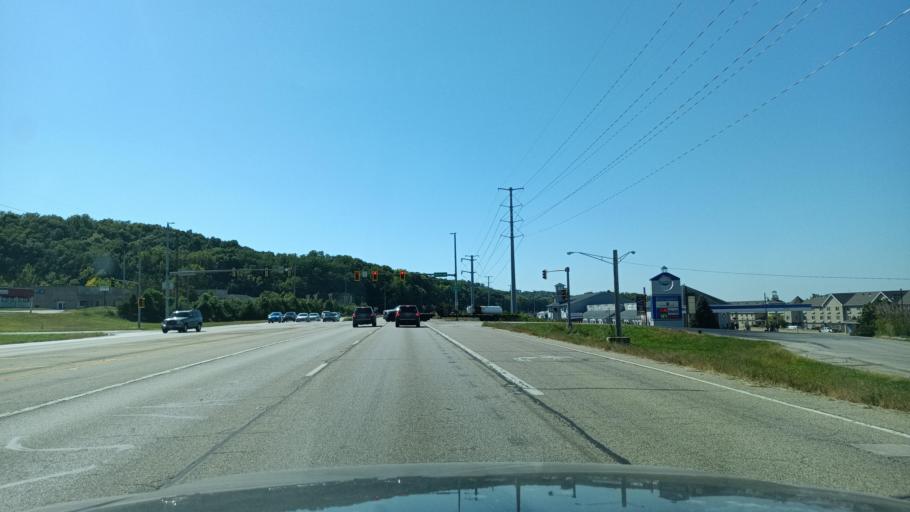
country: US
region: Illinois
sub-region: Peoria County
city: Peoria
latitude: 40.6957
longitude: -89.5409
